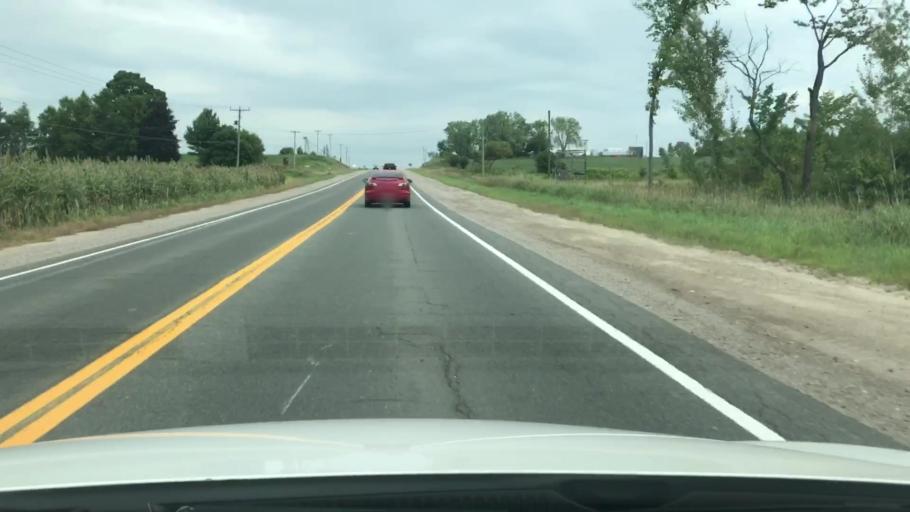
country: CA
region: Ontario
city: Innisfil
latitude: 44.2898
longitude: -79.6108
